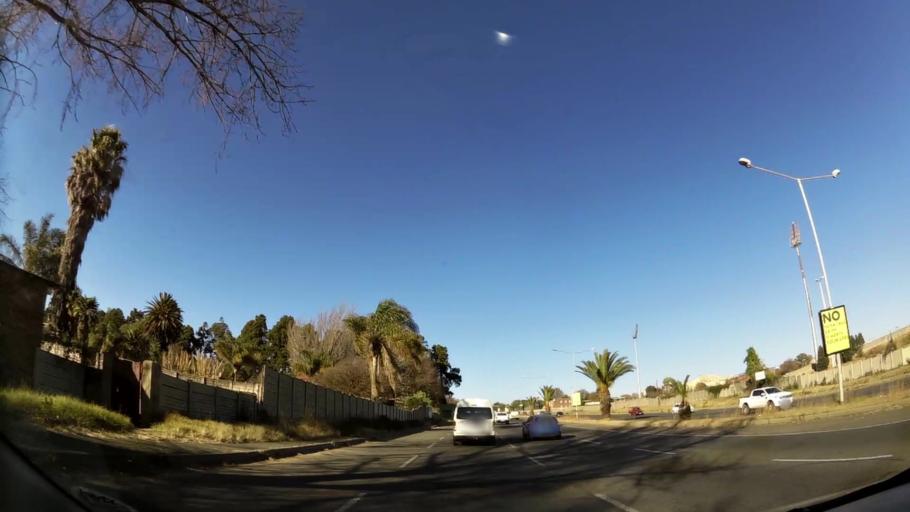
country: ZA
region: Gauteng
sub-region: West Rand District Municipality
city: Krugersdorp
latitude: -26.1012
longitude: 27.7795
